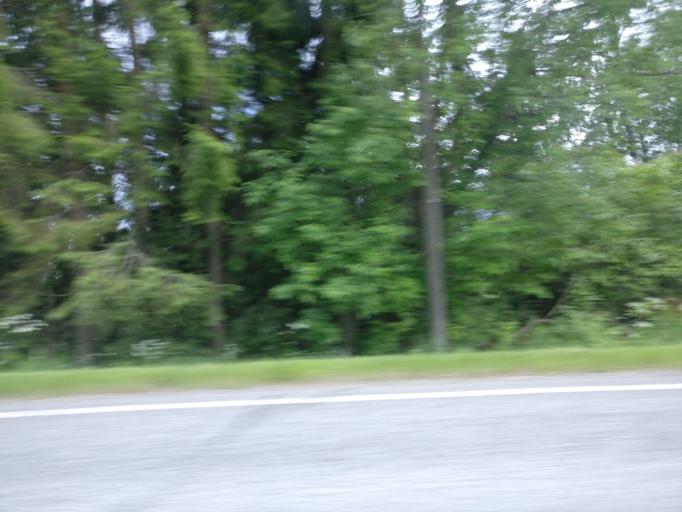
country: FI
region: Southern Savonia
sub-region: Savonlinna
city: Enonkoski
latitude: 61.9724
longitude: 28.9437
